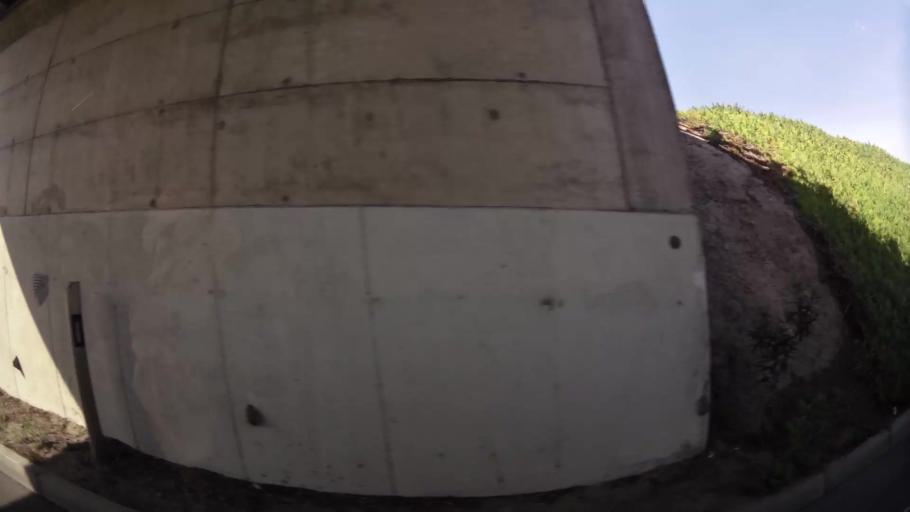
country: CL
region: Santiago Metropolitan
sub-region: Provincia de Santiago
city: Lo Prado
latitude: -33.4159
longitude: -70.7809
